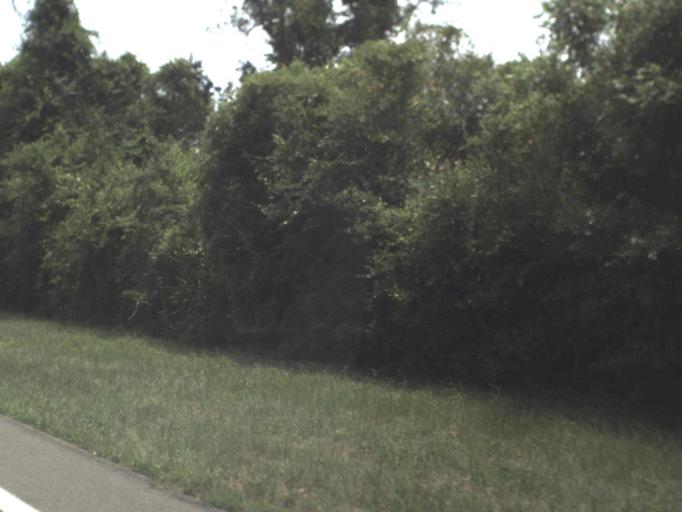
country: US
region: Florida
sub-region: Duval County
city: Atlantic Beach
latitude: 30.4955
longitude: -81.4454
